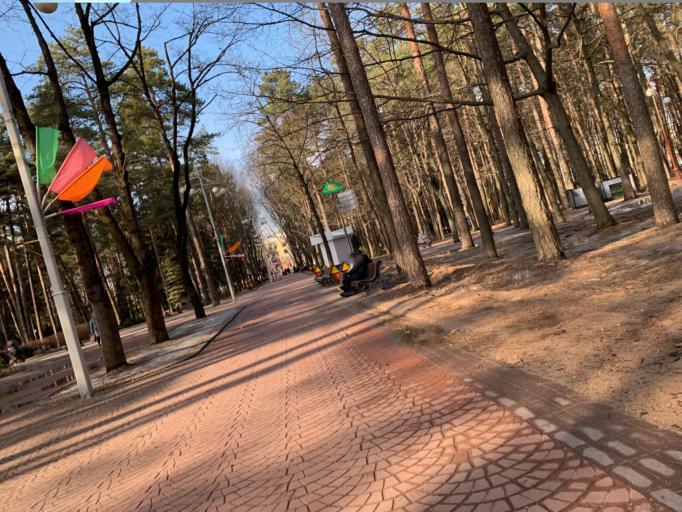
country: BY
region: Minsk
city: Minsk
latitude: 53.9219
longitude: 27.6125
